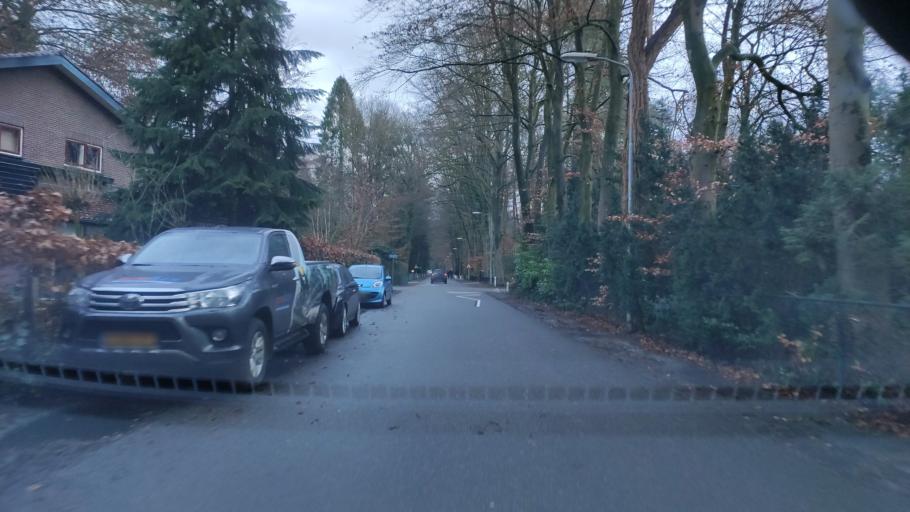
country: NL
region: Gelderland
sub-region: Gemeente Putten
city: Putten
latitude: 52.2576
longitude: 5.6218
